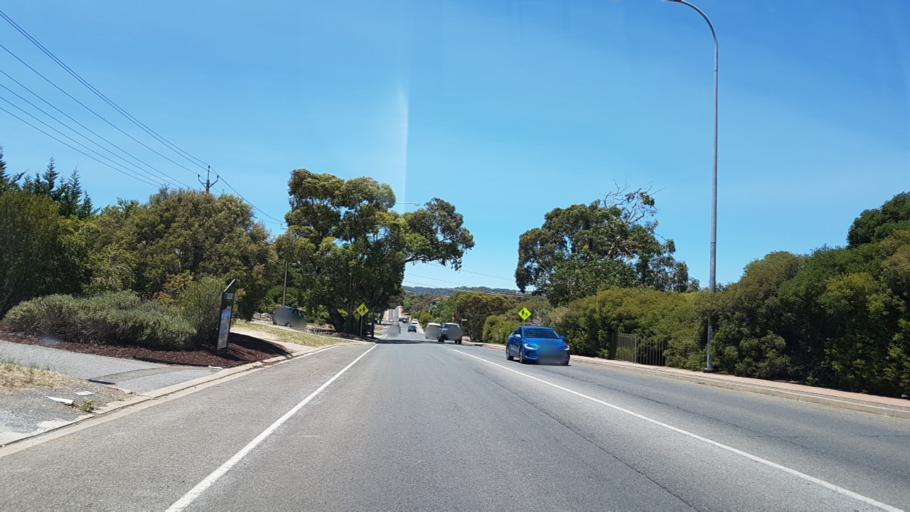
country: AU
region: South Australia
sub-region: Marion
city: Trott Park
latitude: -35.0830
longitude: 138.5502
